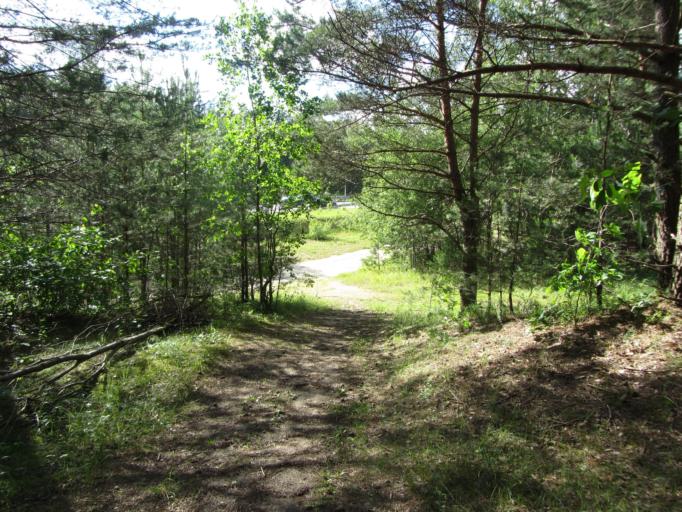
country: LT
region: Vilnius County
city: Lazdynai
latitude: 54.6789
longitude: 25.1961
